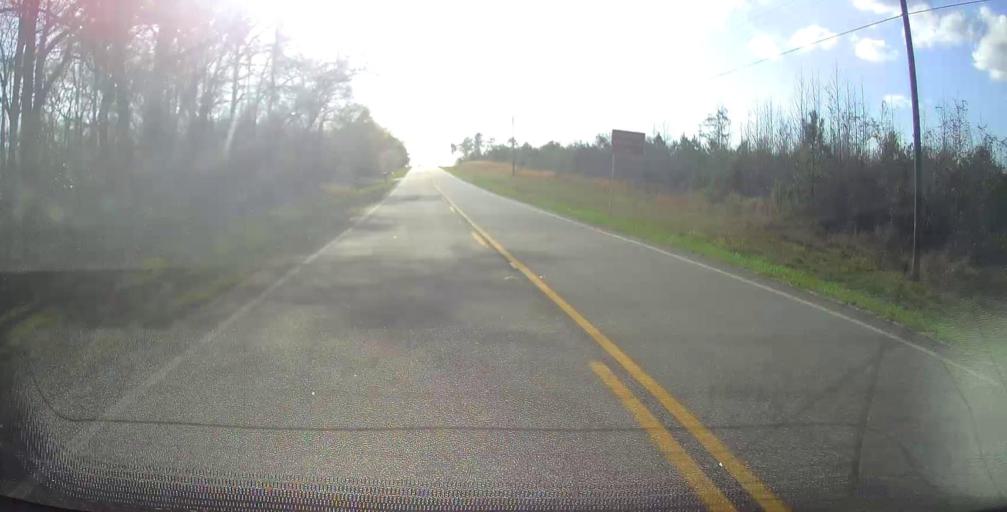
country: US
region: Georgia
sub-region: Wheeler County
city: Alamo
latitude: 32.1597
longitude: -82.7373
